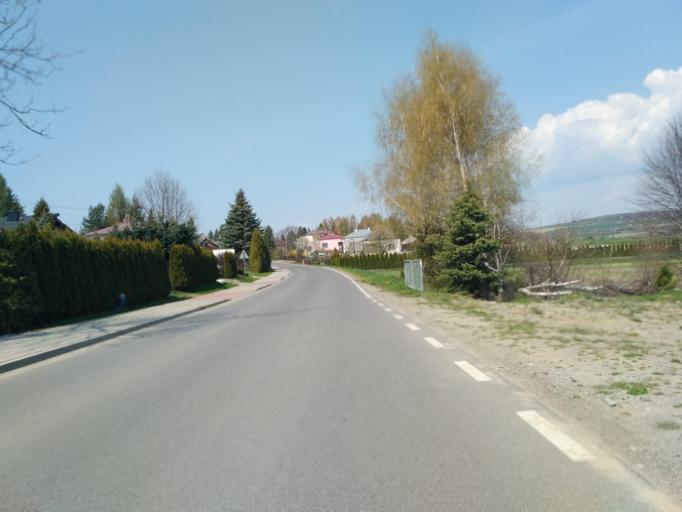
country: PL
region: Subcarpathian Voivodeship
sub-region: Powiat krosnienski
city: Chorkowka
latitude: 49.6527
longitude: 21.6698
